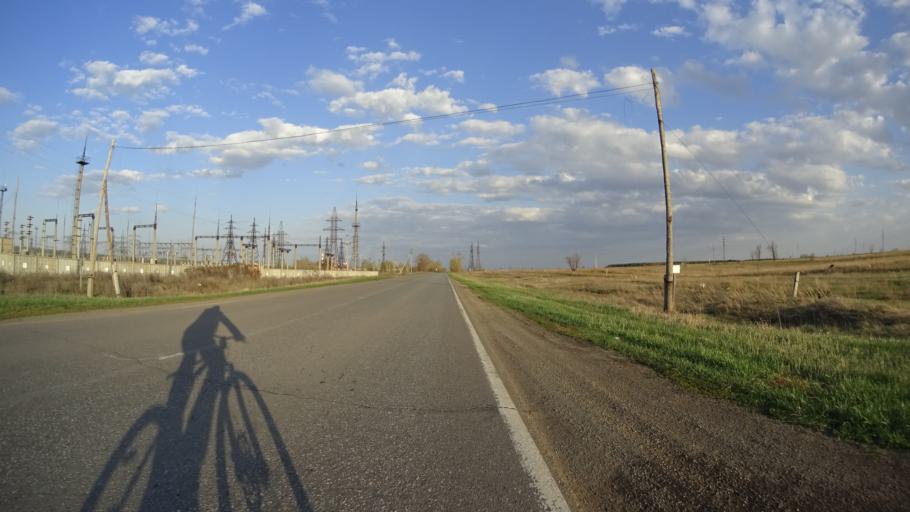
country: RU
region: Chelyabinsk
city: Troitsk
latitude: 54.0587
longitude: 61.5812
